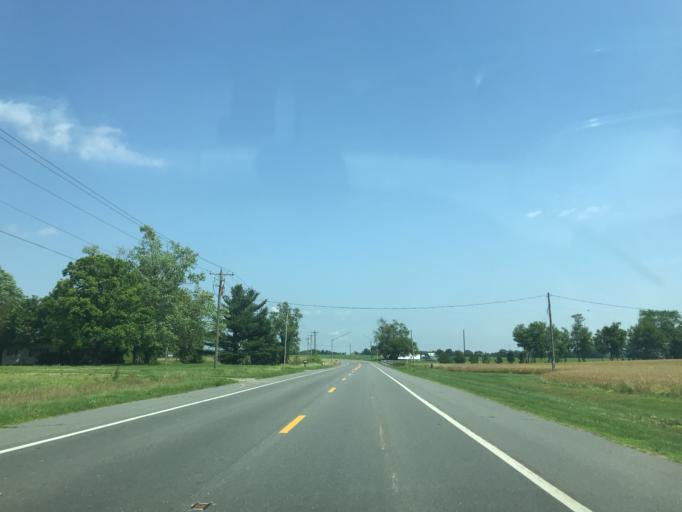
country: US
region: Maryland
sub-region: Dorchester County
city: Hurlock
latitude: 38.5947
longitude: -75.8958
